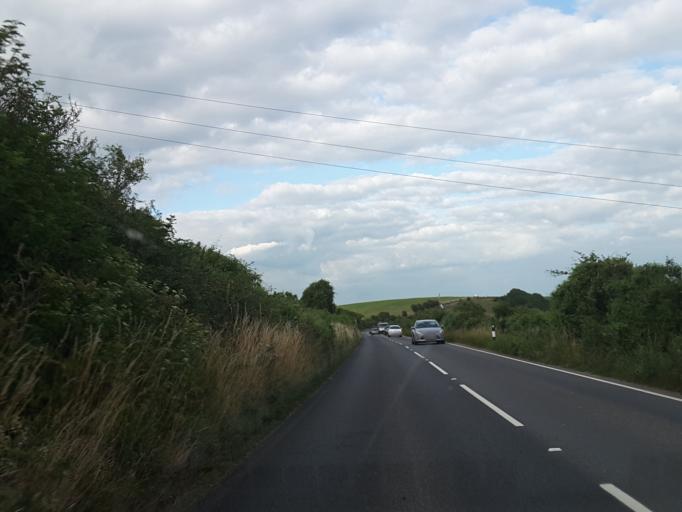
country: GB
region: England
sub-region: Isle of Wight
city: Newchurch
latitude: 50.6816
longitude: -1.2226
